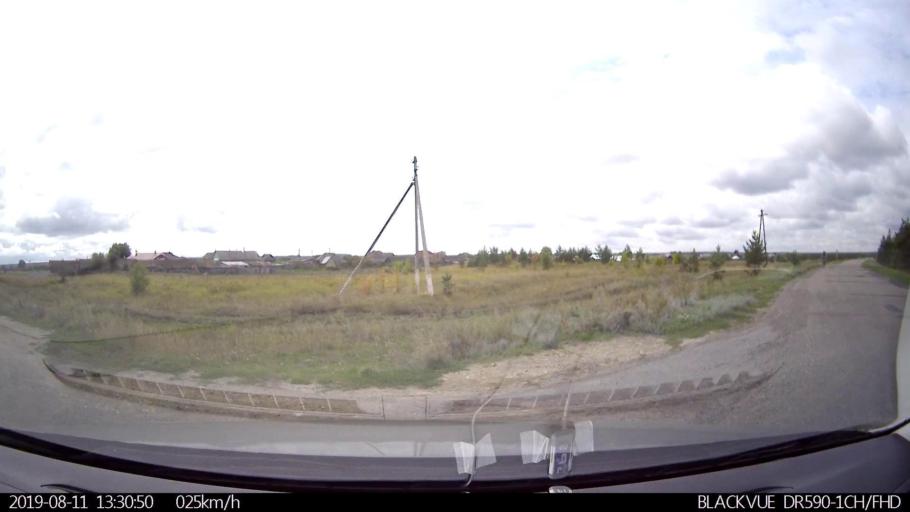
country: RU
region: Ulyanovsk
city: Ignatovka
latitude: 53.8606
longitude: 47.5997
